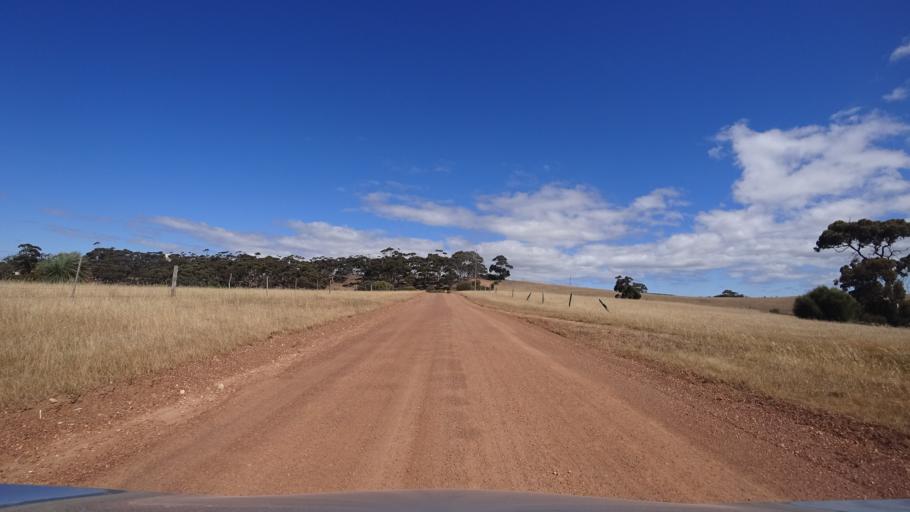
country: AU
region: South Australia
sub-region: Kangaroo Island
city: Kingscote
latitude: -35.6889
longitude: 136.9803
